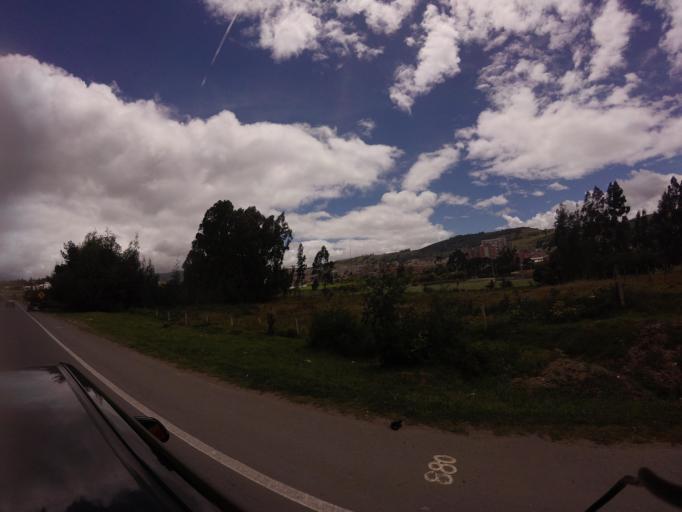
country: CO
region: Boyaca
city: Tunja
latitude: 5.5667
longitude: -73.3311
